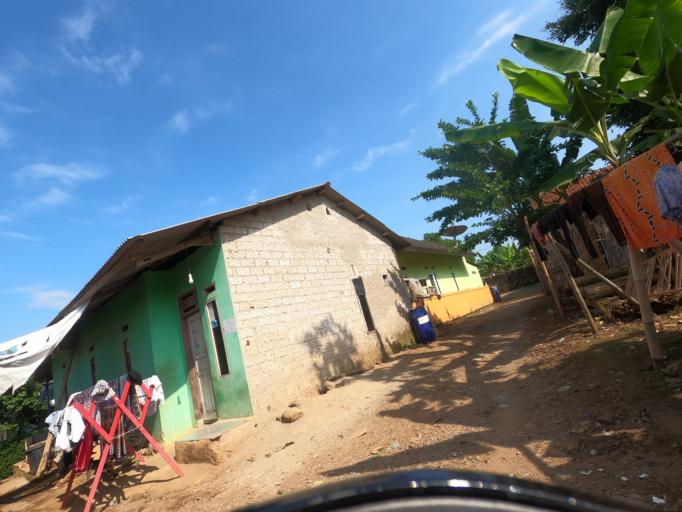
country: ID
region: West Java
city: Lembang
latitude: -6.5812
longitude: 107.7822
